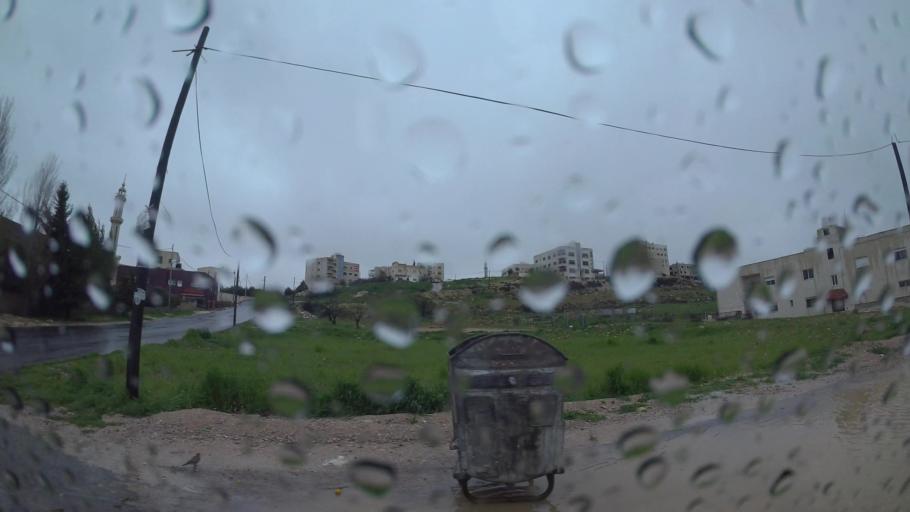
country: JO
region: Amman
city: Al Jubayhah
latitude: 32.0388
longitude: 35.8943
